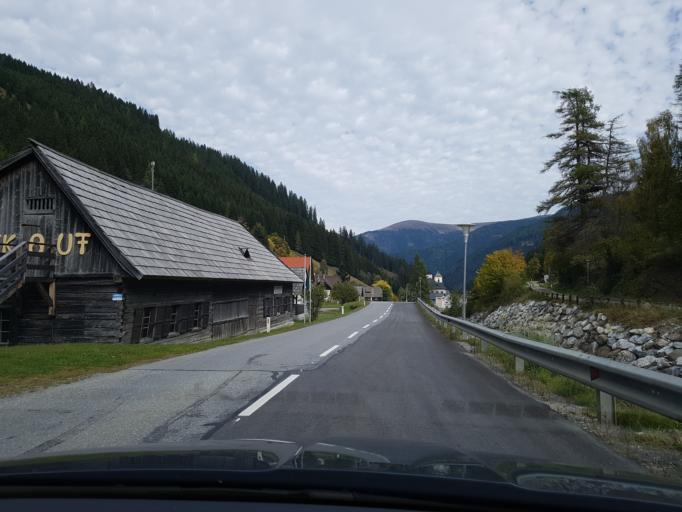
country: AT
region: Salzburg
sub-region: Politischer Bezirk Tamsweg
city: Ramingstein
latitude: 46.9603
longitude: 13.8826
